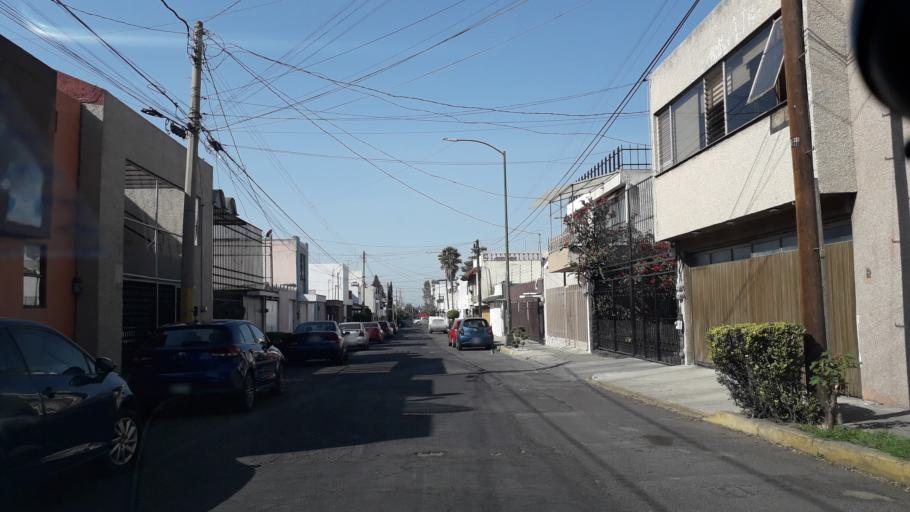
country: MX
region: Puebla
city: Puebla
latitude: 19.0285
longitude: -98.2152
